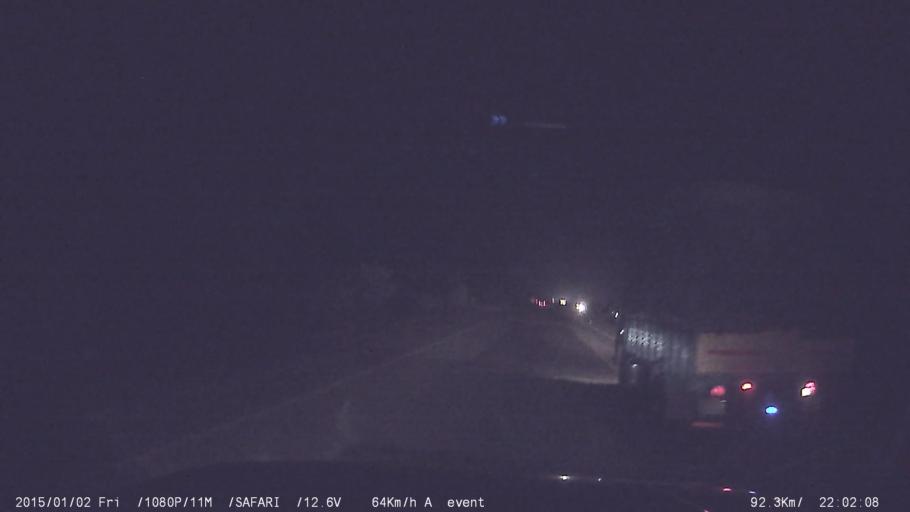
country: IN
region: Tamil Nadu
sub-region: Vellore
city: Walajapet
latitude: 12.9018
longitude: 79.4316
